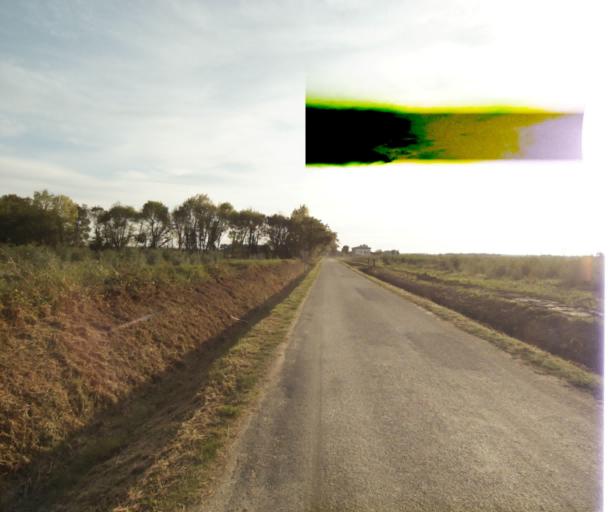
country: FR
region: Midi-Pyrenees
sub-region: Departement du Tarn-et-Garonne
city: Labastide-Saint-Pierre
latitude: 43.8975
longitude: 1.3591
